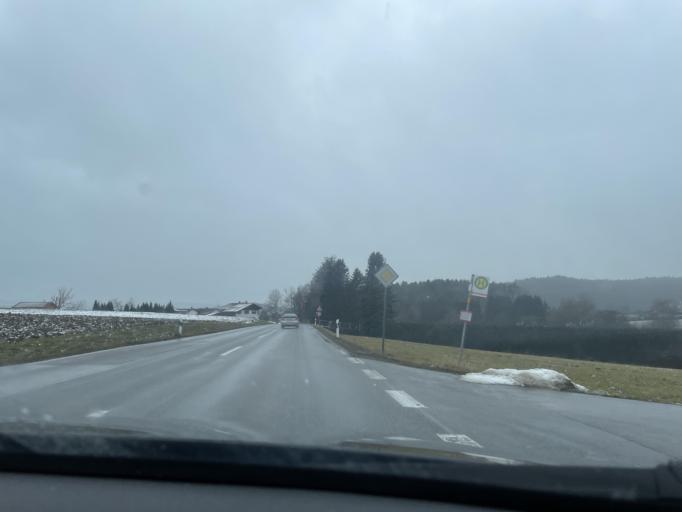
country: DE
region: Bavaria
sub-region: Upper Palatinate
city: Kotzting
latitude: 49.1980
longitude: 12.8563
